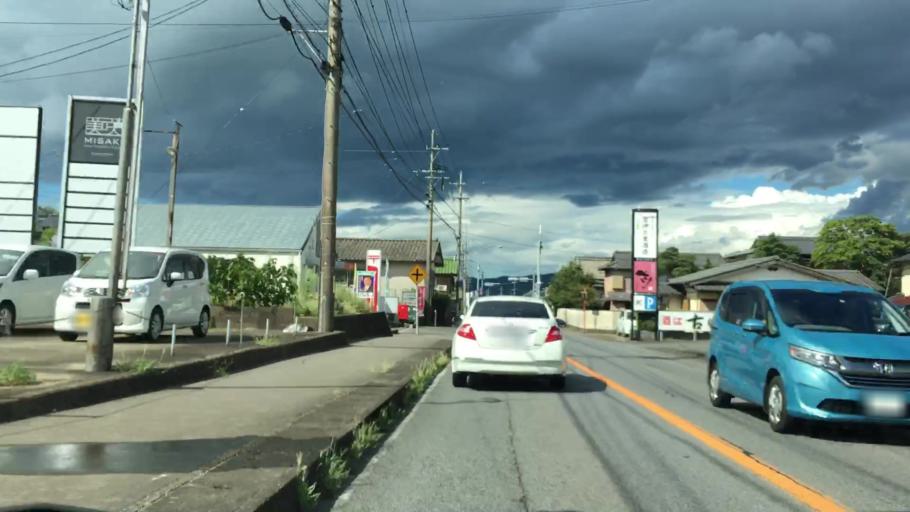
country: JP
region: Saga Prefecture
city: Imaricho-ko
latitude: 33.2444
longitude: 129.8509
